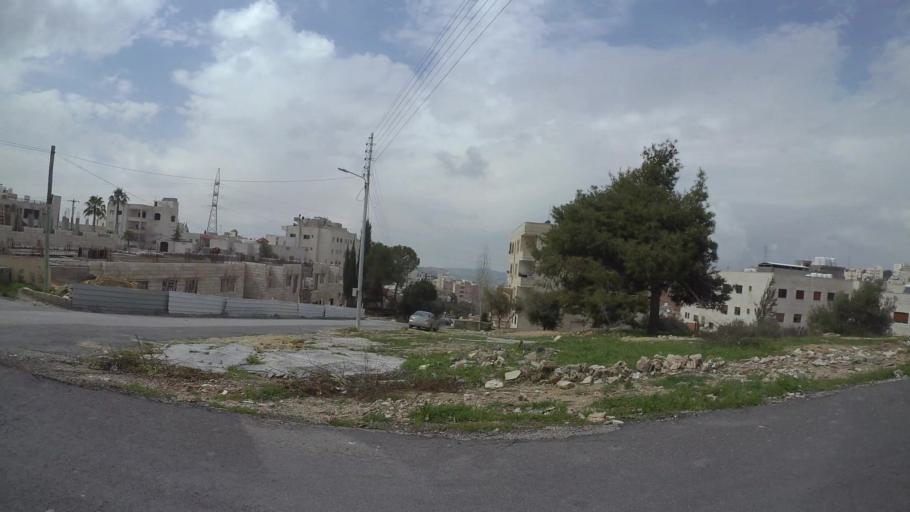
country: JO
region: Amman
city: Umm as Summaq
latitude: 31.8979
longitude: 35.8355
